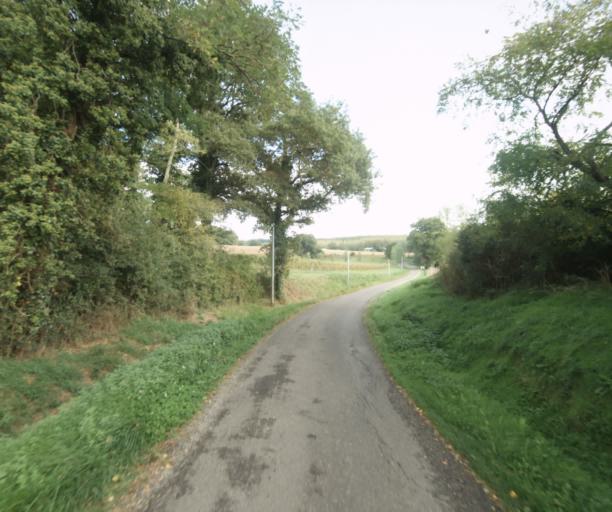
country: FR
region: Midi-Pyrenees
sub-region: Departement du Gers
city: Cazaubon
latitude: 43.8670
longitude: -0.1219
